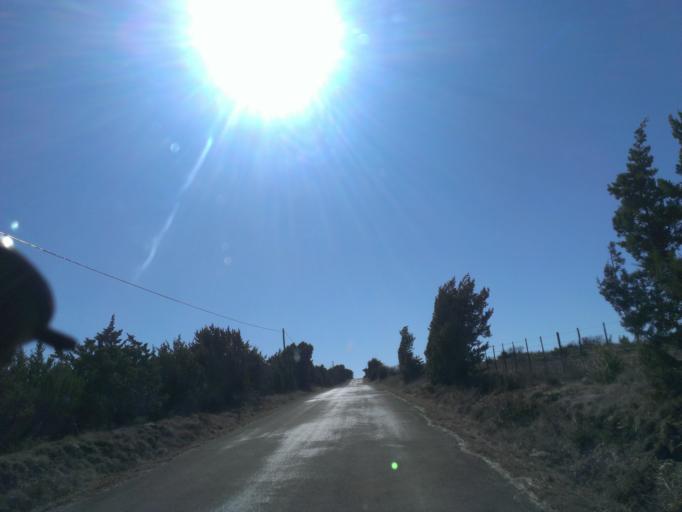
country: US
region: Texas
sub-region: Lampasas County
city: Lampasas
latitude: 30.9141
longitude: -98.1486
